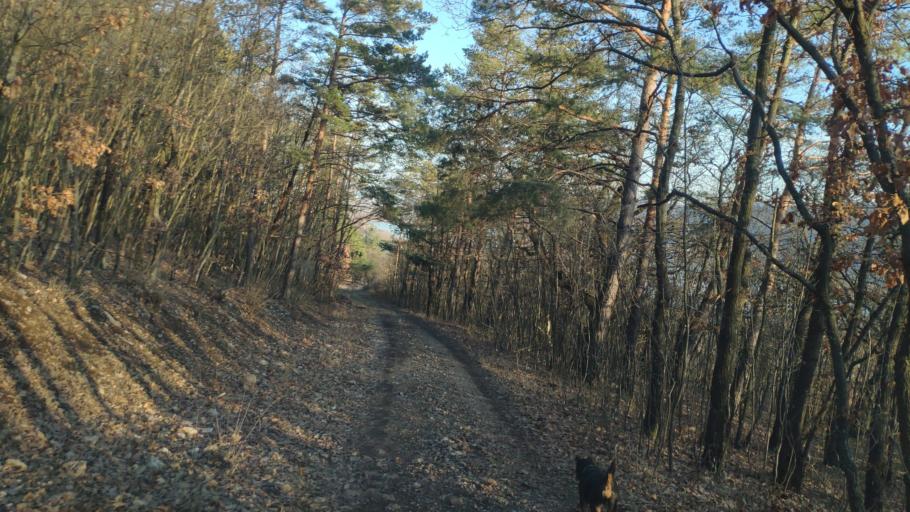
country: SK
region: Kosicky
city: Medzev
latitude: 48.6036
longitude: 20.7306
